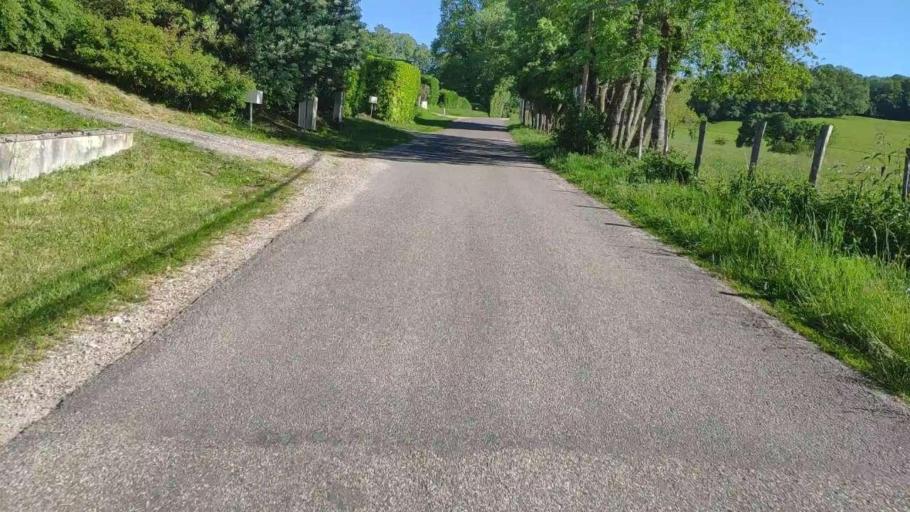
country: FR
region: Franche-Comte
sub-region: Departement du Jura
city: Lons-le-Saunier
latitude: 46.7226
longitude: 5.5543
